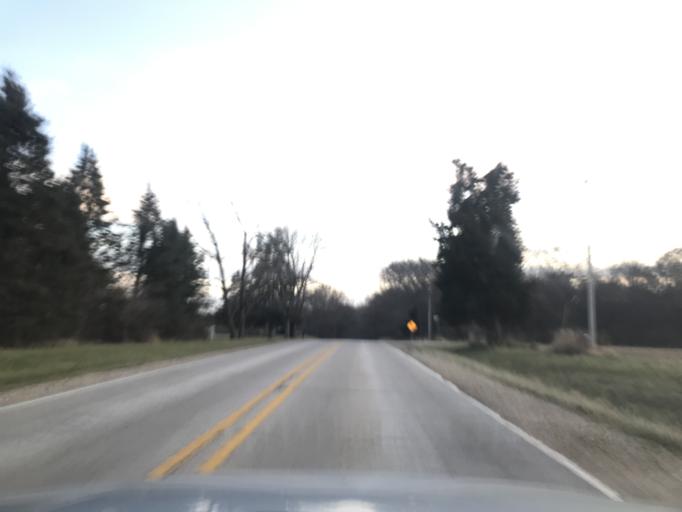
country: US
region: Illinois
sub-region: Henderson County
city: Oquawka
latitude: 40.8989
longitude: -90.8645
